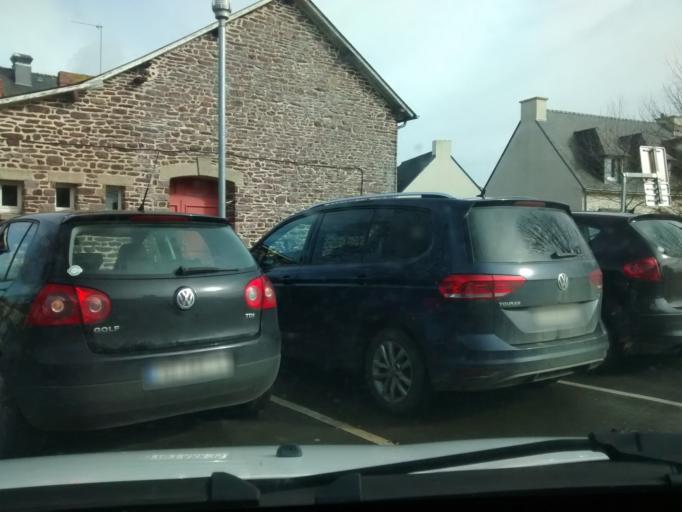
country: FR
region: Brittany
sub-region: Departement d'Ille-et-Vilaine
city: Nouvoitou
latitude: 48.0425
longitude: -1.5465
